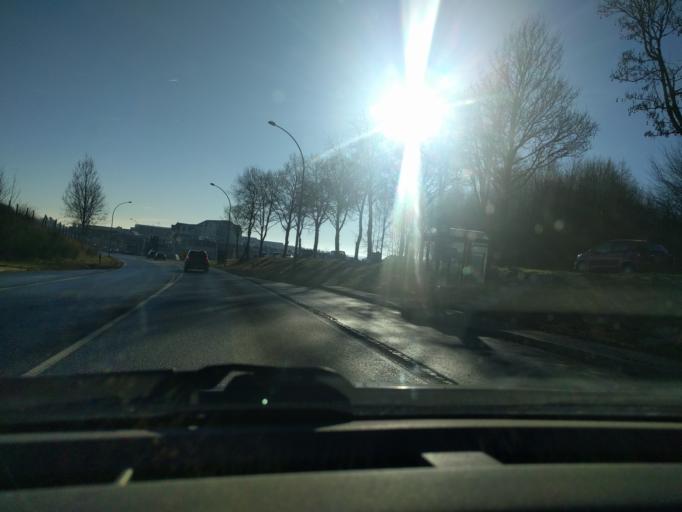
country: LU
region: Diekirch
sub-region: Canton de Clervaux
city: Weiswampach
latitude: 50.1509
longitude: 6.0540
